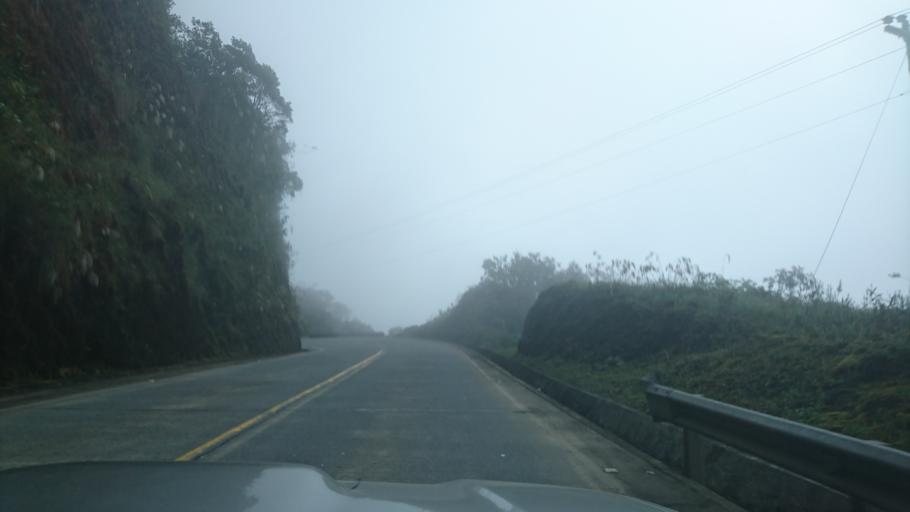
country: BO
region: La Paz
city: Coroico
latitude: -16.2852
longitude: -67.8291
